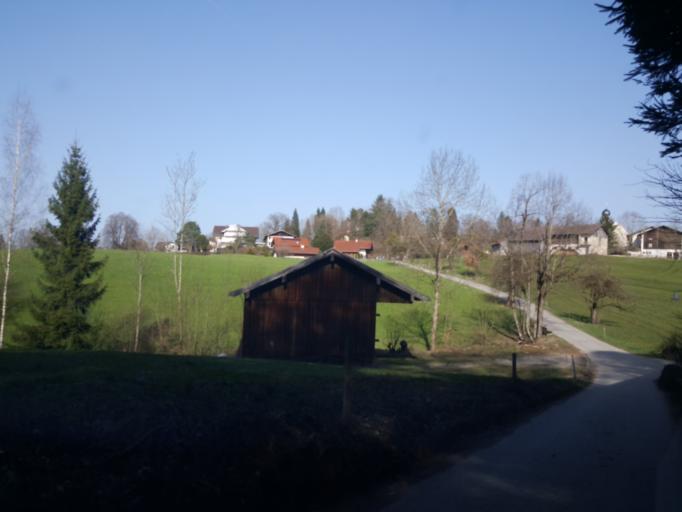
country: DE
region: Bavaria
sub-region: Upper Bavaria
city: Bad Heilbrunn
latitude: 47.7455
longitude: 11.4474
